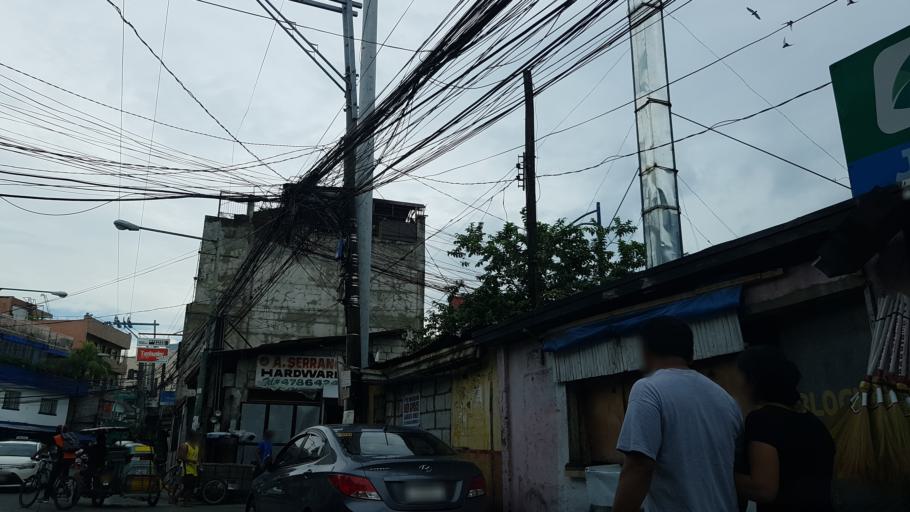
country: PH
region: Calabarzon
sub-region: Province of Rizal
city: Pateros
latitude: 14.5421
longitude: 121.0585
